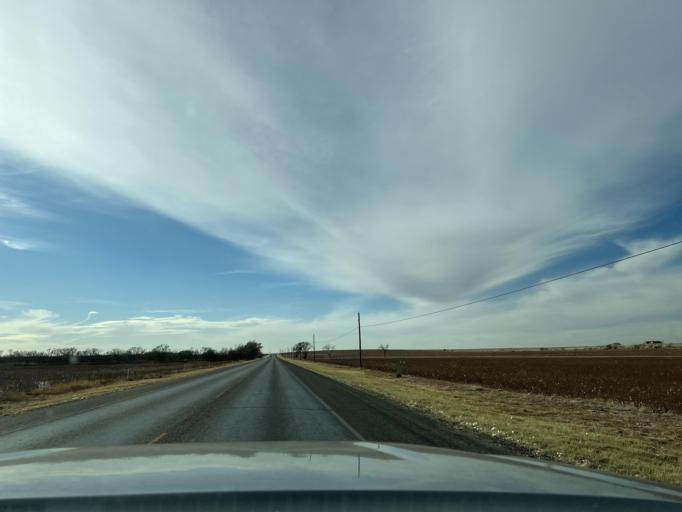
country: US
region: Texas
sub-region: Fisher County
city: Roby
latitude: 32.7409
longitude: -100.4769
